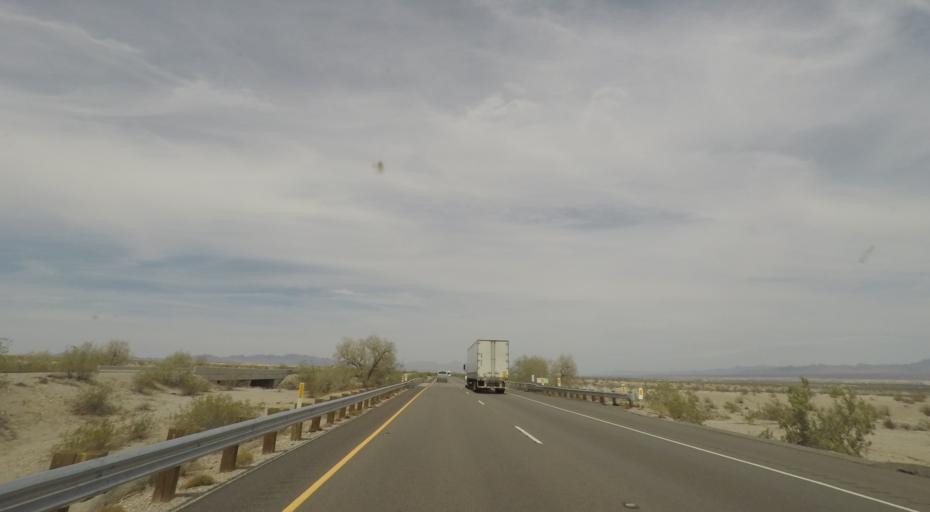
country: US
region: California
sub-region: San Bernardino County
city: Needles
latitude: 34.7902
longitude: -114.5859
